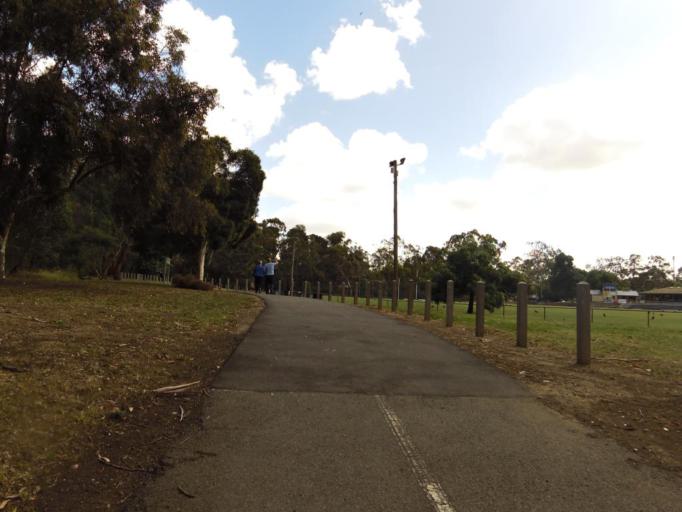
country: AU
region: Victoria
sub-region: Nillumbik
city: Eltham North
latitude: -37.7157
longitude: 145.1442
